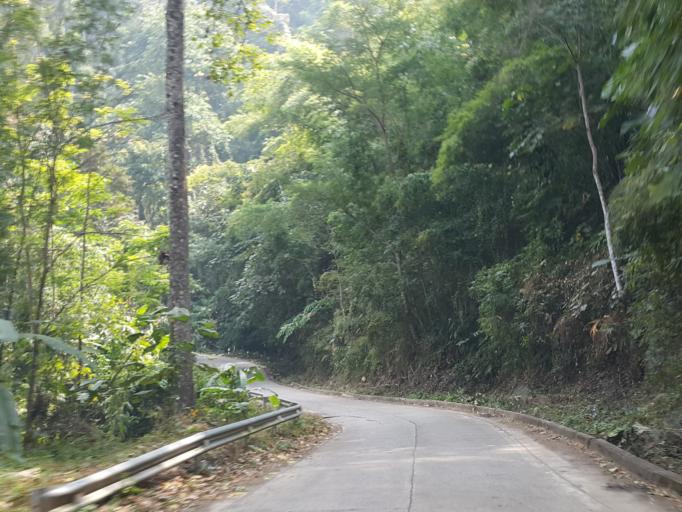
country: TH
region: Chiang Mai
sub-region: Amphoe Chiang Dao
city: Chiang Dao
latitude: 19.4106
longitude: 98.8710
